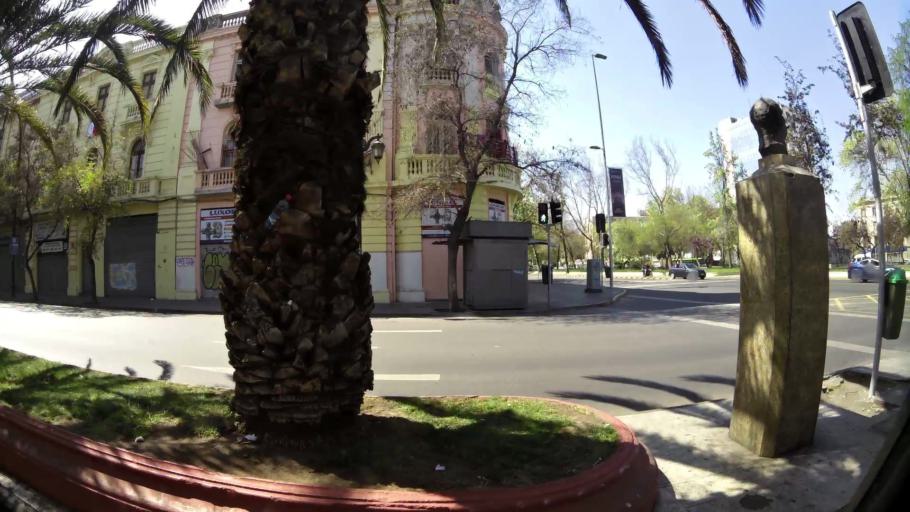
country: CL
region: Santiago Metropolitan
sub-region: Provincia de Santiago
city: Santiago
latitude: -33.4467
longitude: -70.6646
